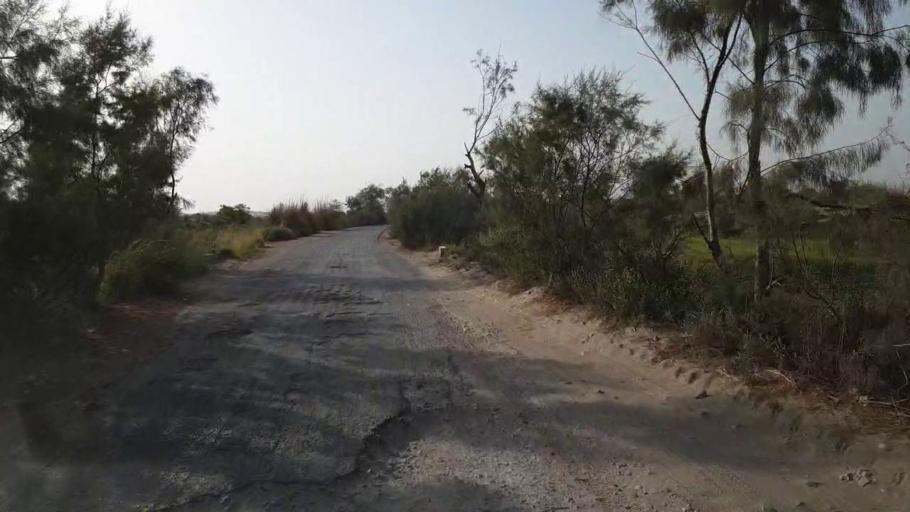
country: PK
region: Sindh
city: Jam Sahib
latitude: 26.4906
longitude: 68.8586
